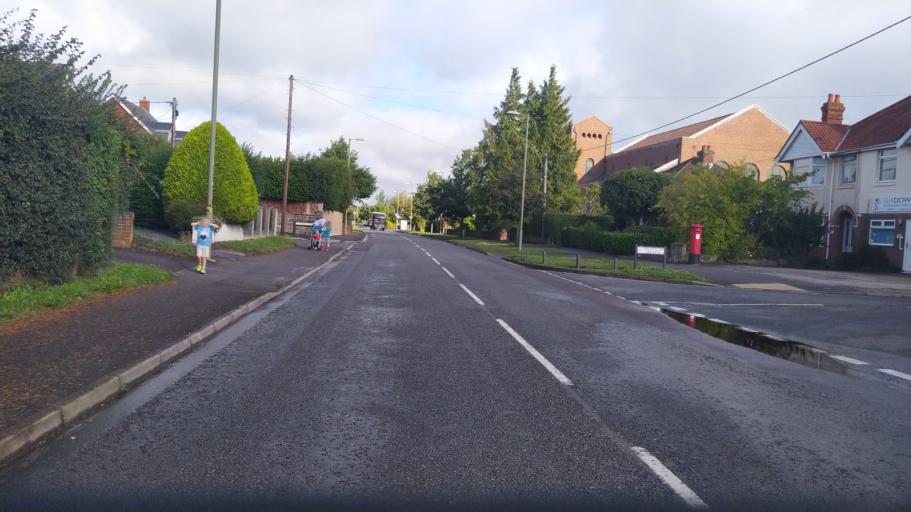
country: GB
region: England
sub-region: Hampshire
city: Totton
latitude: 50.9218
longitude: -1.4939
